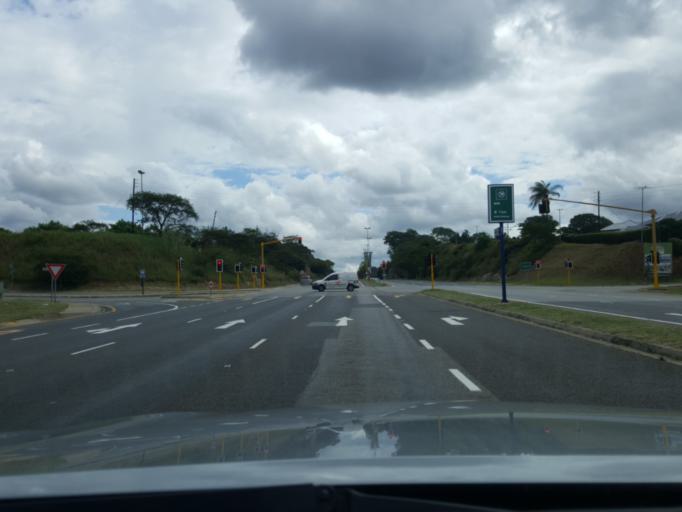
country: ZA
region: Mpumalanga
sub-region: Ehlanzeni District
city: Nelspruit
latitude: -25.4601
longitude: 30.9458
